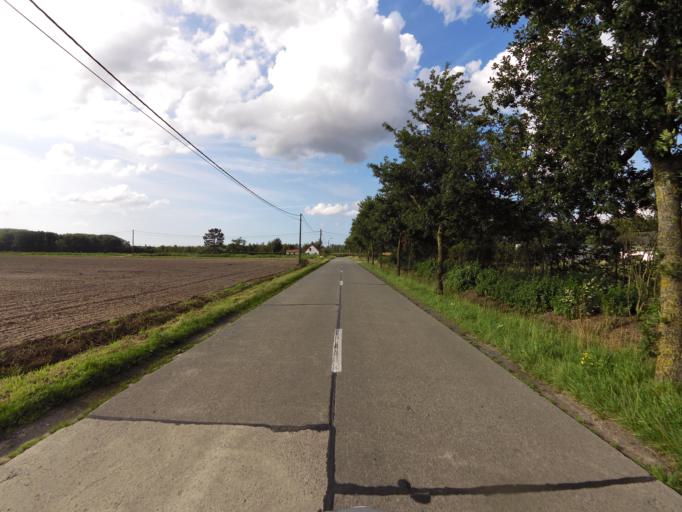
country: BE
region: Flanders
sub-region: Provincie West-Vlaanderen
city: Wingene
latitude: 51.0905
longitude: 3.2765
